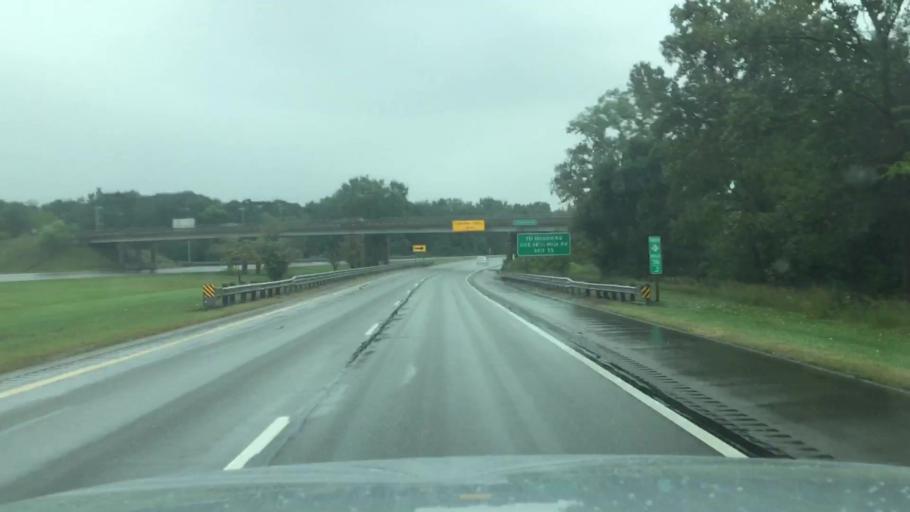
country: US
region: Michigan
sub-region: Macomb County
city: Utica
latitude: 42.6074
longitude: -83.0156
